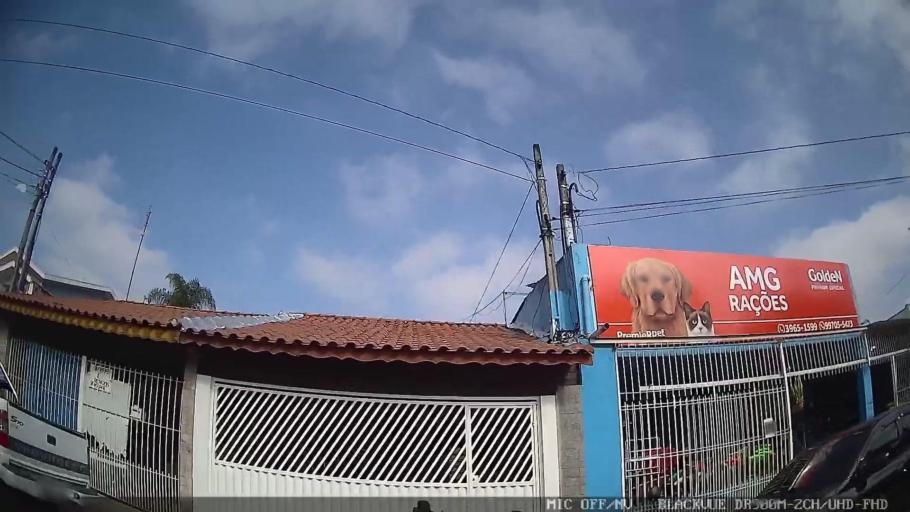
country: BR
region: Sao Paulo
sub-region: Jacarei
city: Jacarei
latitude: -23.3105
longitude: -46.0100
